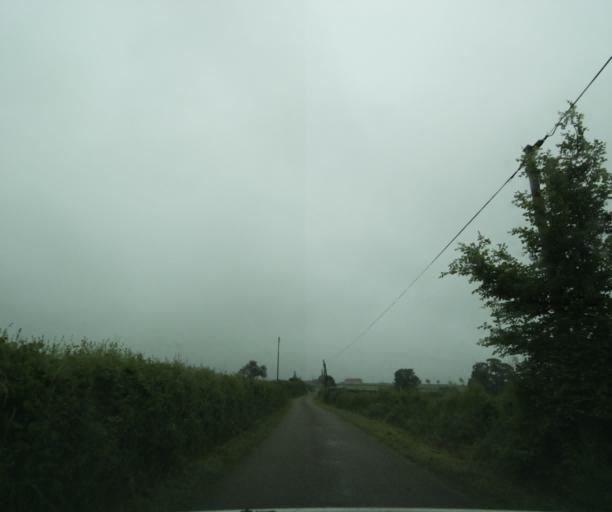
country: FR
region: Bourgogne
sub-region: Departement de Saone-et-Loire
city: Charolles
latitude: 46.4180
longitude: 4.3791
